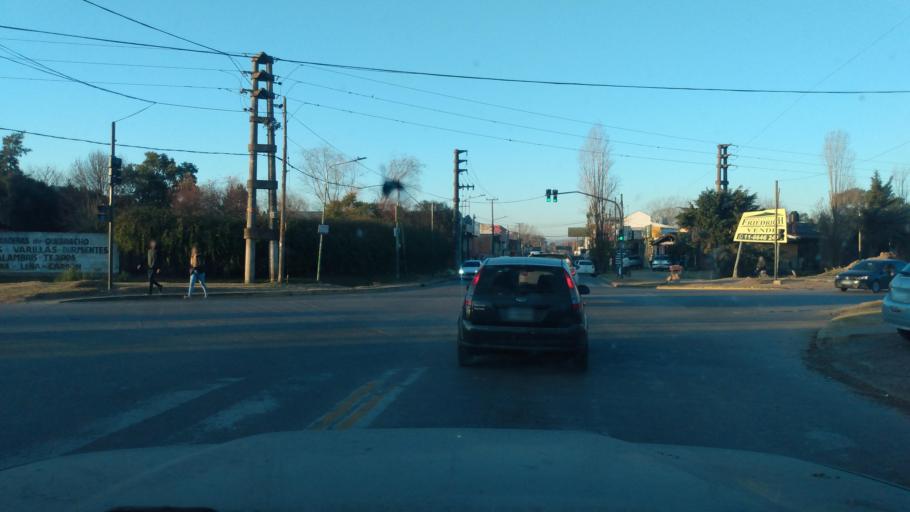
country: AR
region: Buenos Aires
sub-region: Partido de General Rodriguez
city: General Rodriguez
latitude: -34.5989
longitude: -58.9422
